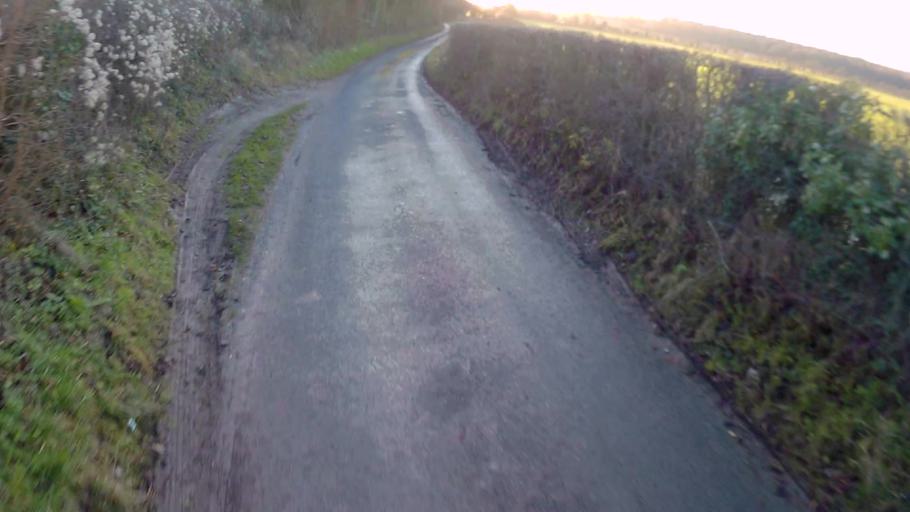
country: GB
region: England
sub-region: Hampshire
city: Basingstoke
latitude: 51.2161
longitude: -1.1298
